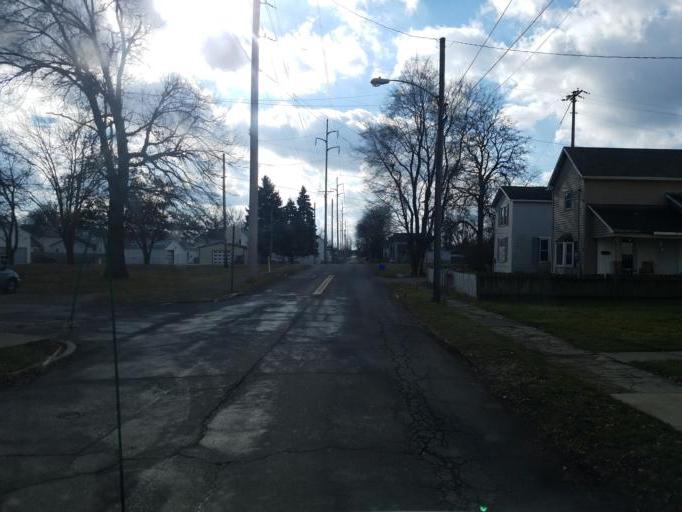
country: US
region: Ohio
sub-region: Marion County
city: Marion
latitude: 40.5836
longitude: -83.1455
